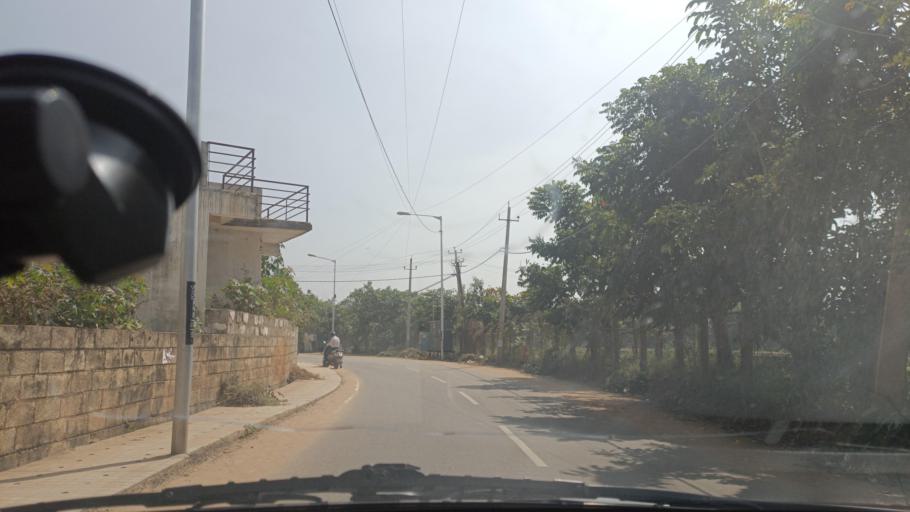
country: IN
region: Karnataka
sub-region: Bangalore Urban
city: Yelahanka
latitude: 13.1160
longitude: 77.6183
